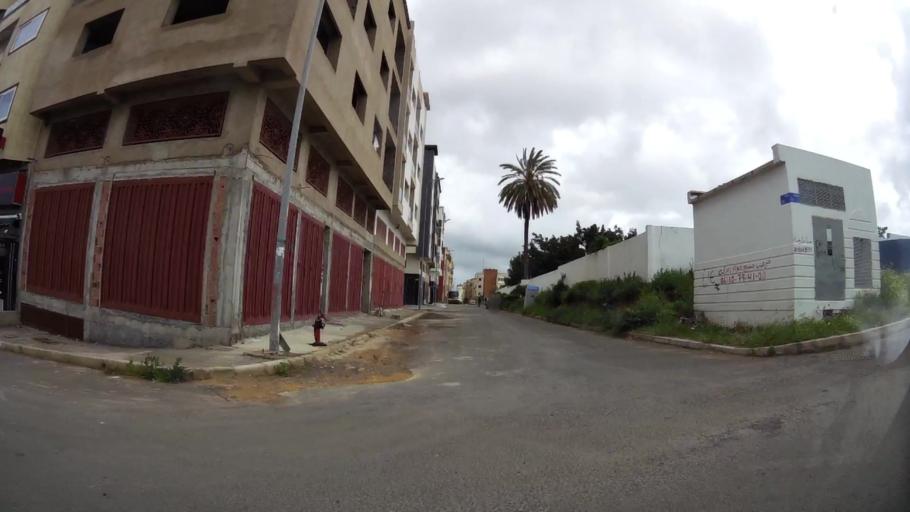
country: MA
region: Grand Casablanca
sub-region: Casablanca
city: Casablanca
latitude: 33.5326
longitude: -7.5975
